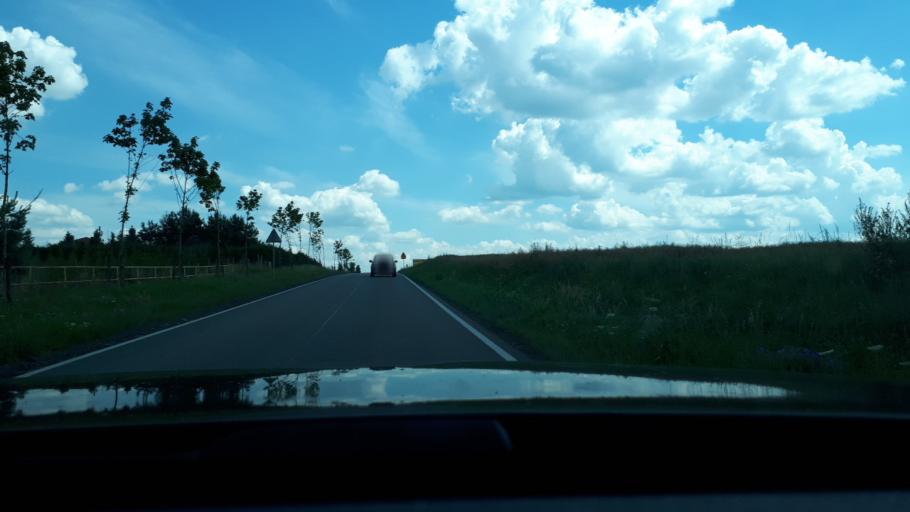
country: PL
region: Warmian-Masurian Voivodeship
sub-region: Powiat olsztynski
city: Olsztynek
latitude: 53.5843
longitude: 20.3062
